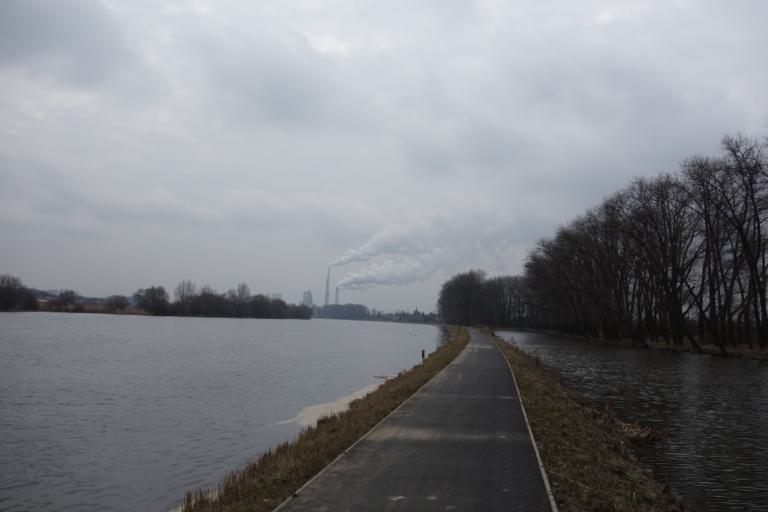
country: CZ
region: Central Bohemia
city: Horni Pocaply
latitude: 50.4340
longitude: 14.3785
